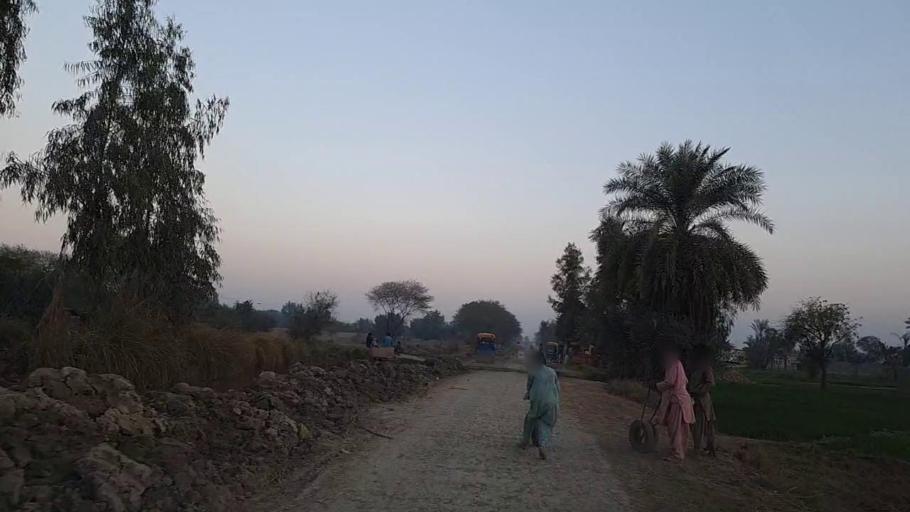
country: PK
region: Sindh
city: Naushahro Firoz
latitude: 26.7975
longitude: 68.0352
